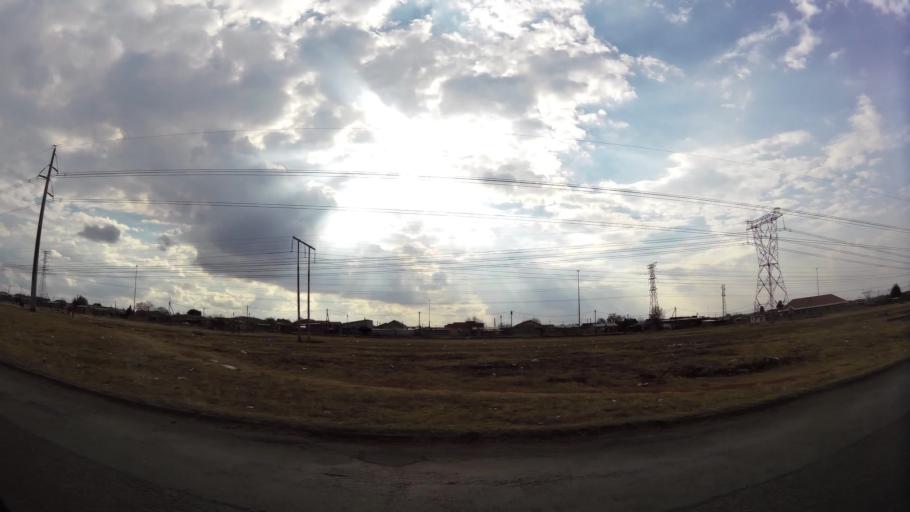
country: ZA
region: Gauteng
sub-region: Sedibeng District Municipality
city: Vanderbijlpark
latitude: -26.6771
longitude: 27.8752
